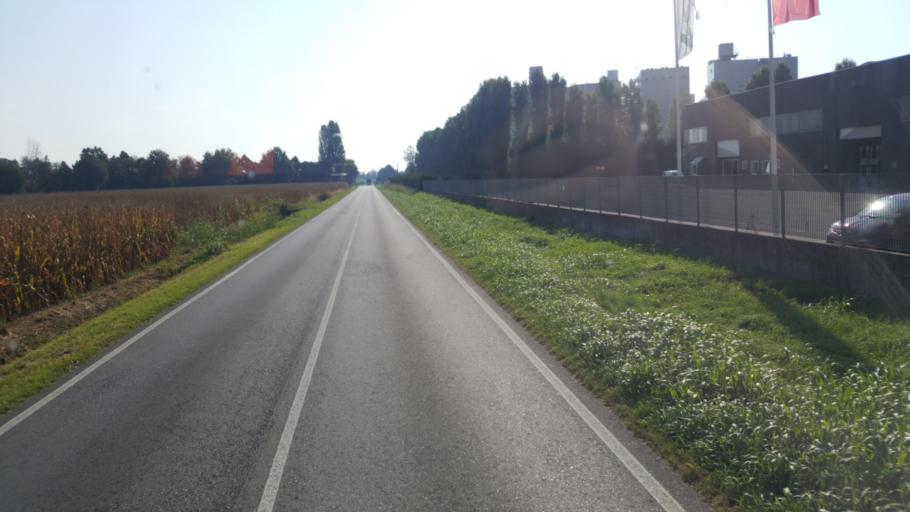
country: IT
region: Lombardy
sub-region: Provincia di Cremona
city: Casalbuttano
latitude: 45.2583
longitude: 9.9554
